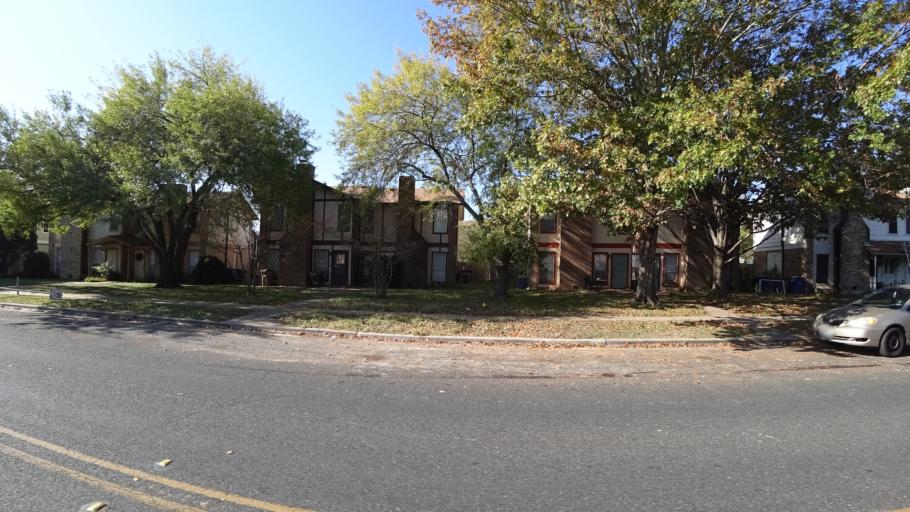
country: US
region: Texas
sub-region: Travis County
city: Barton Creek
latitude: 30.2315
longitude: -97.8460
